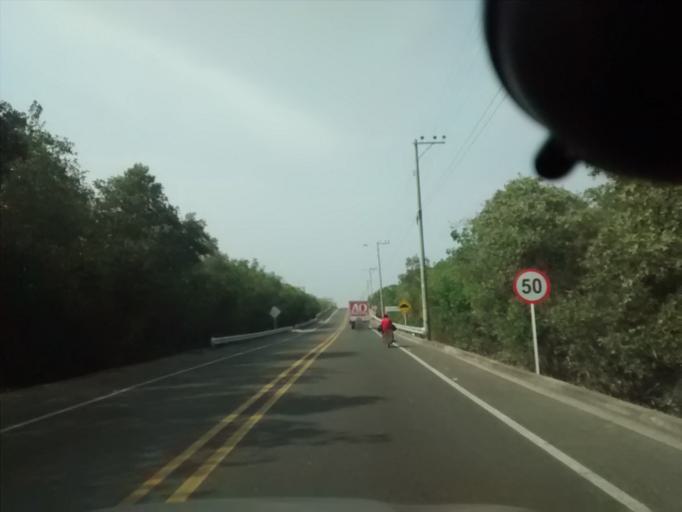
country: CO
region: Bolivar
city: Cartagena
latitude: 10.4825
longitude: -75.4874
